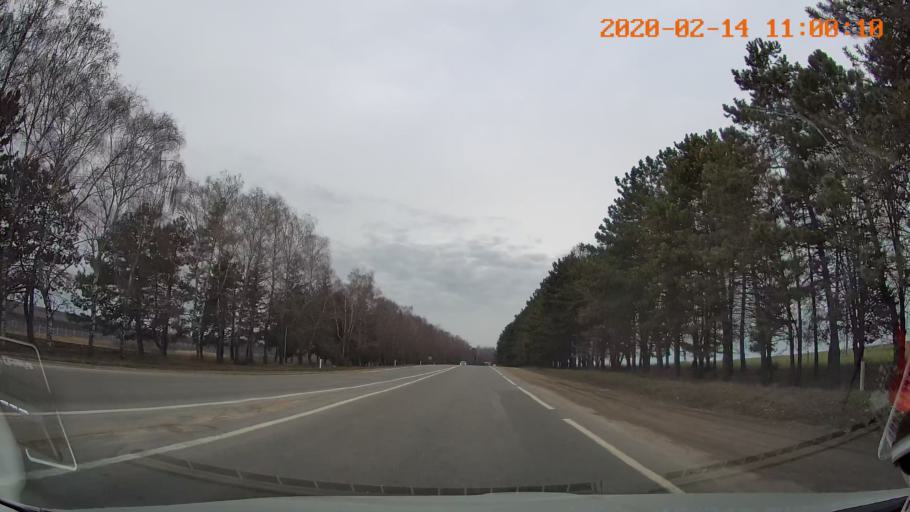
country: MD
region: Raionul Edinet
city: Edinet
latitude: 48.1509
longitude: 27.3411
